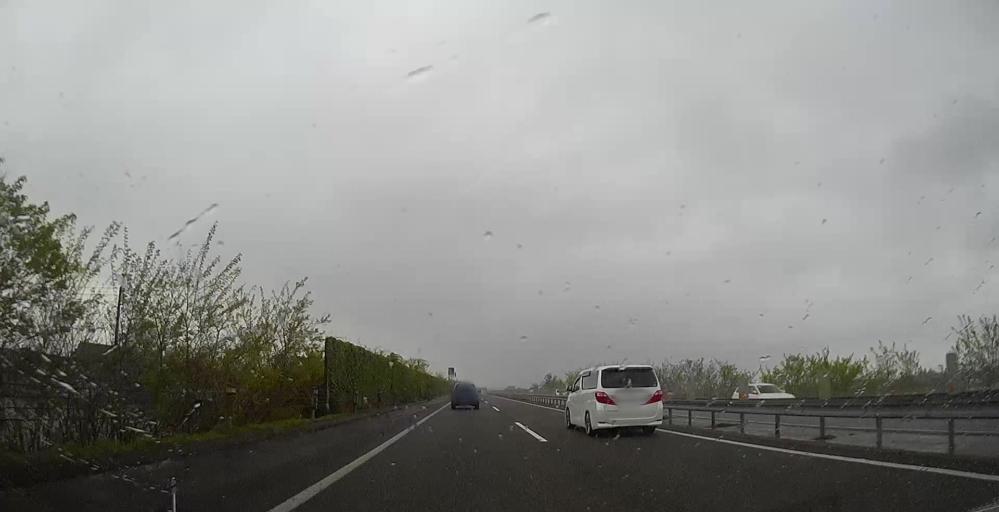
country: JP
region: Niigata
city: Maki
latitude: 37.7523
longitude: 138.9408
